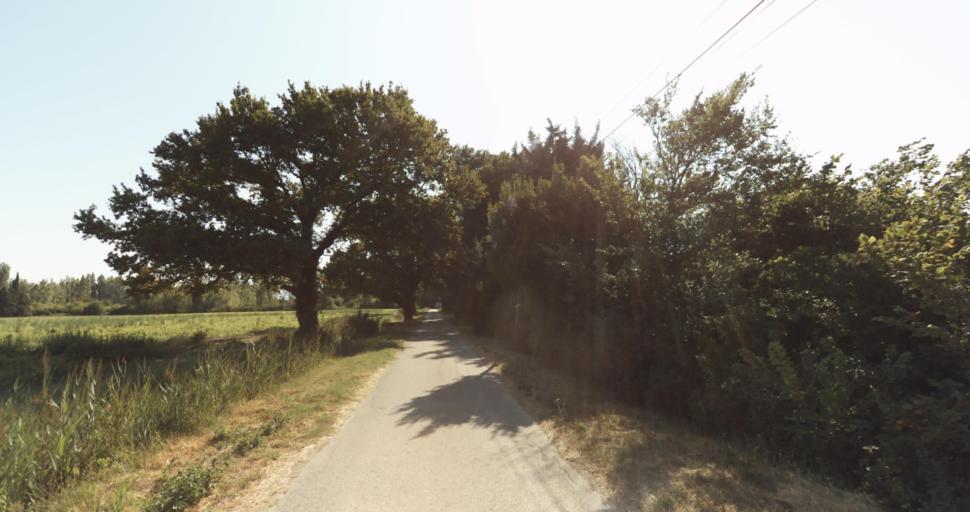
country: FR
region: Provence-Alpes-Cote d'Azur
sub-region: Departement du Vaucluse
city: Althen-des-Paluds
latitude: 44.0199
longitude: 4.9581
